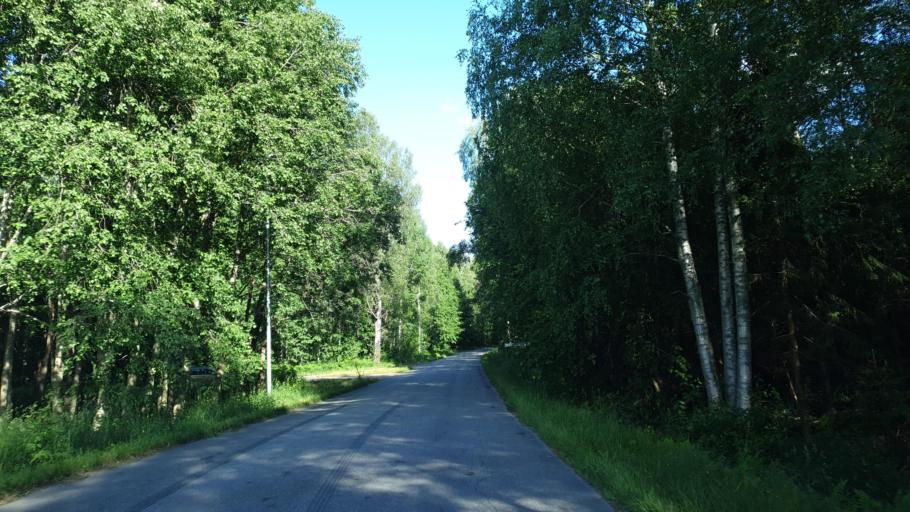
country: SE
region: Dalarna
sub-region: Avesta Kommun
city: Avesta
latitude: 60.1292
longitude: 16.2616
